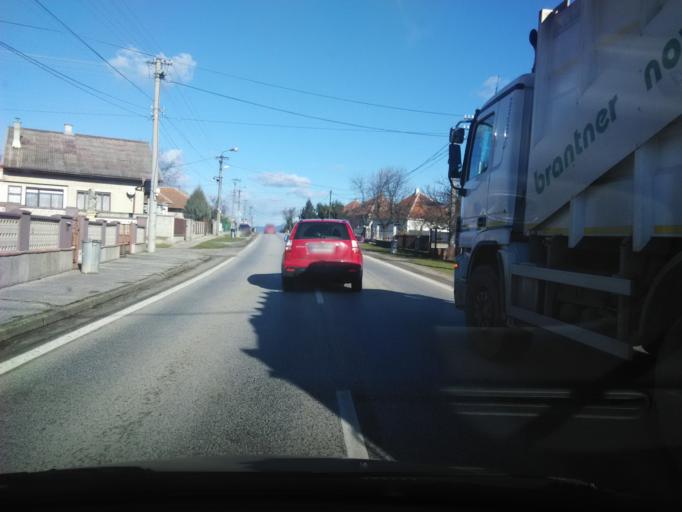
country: SK
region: Nitriansky
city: Surany
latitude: 48.1864
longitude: 18.1484
